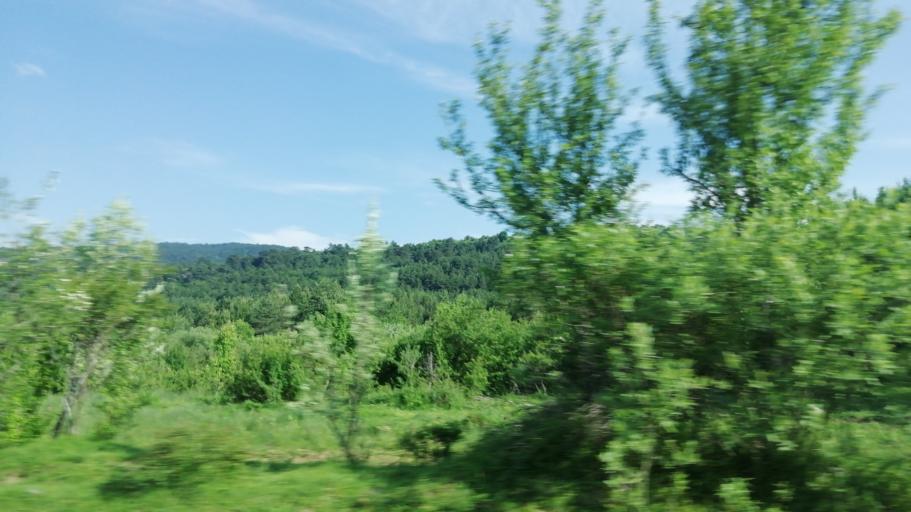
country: TR
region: Karabuk
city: Eskipazar
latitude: 41.0805
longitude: 32.5613
